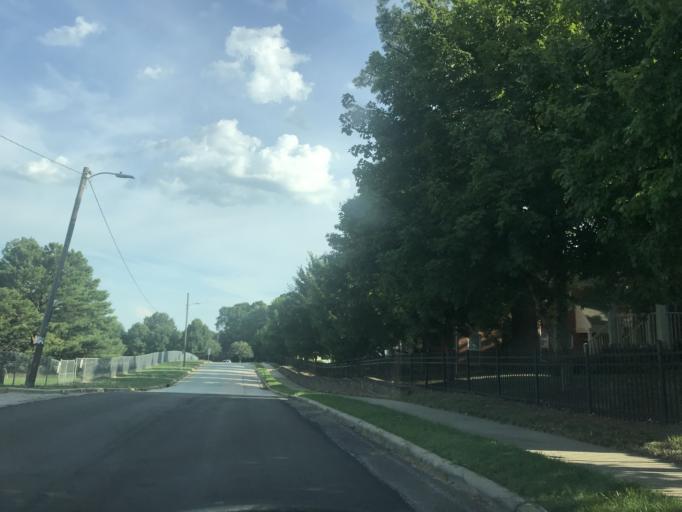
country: US
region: North Carolina
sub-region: Wake County
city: Raleigh
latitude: 35.7696
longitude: -78.6270
